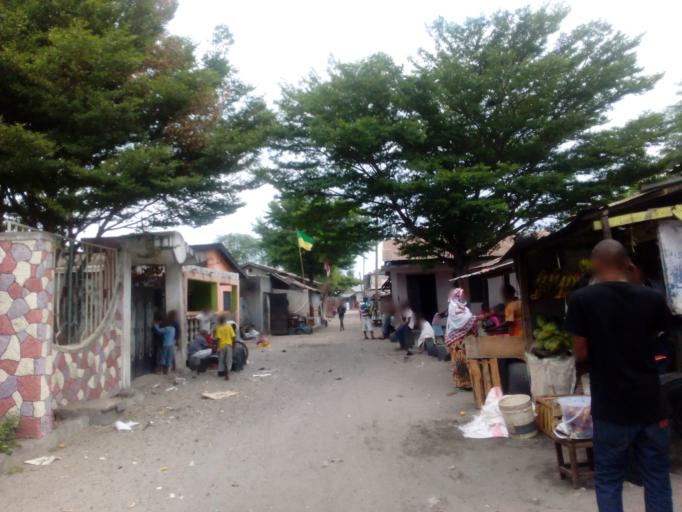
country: TZ
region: Dar es Salaam
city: Dar es Salaam
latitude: -6.8516
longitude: 39.2563
